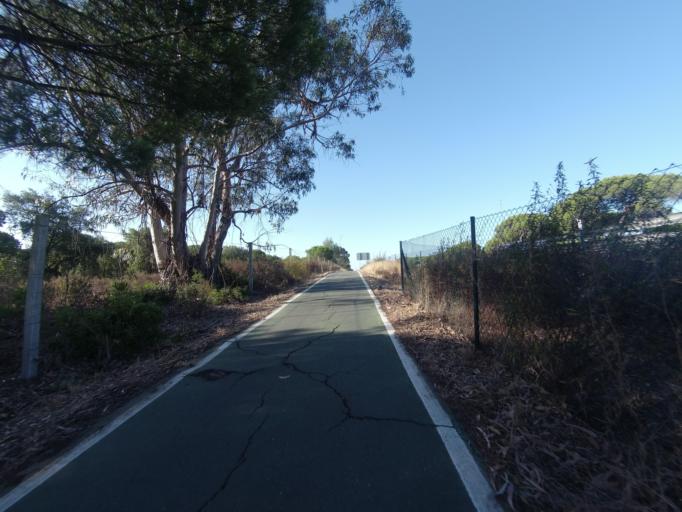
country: ES
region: Andalusia
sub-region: Provincia de Huelva
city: Aljaraque
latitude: 37.2417
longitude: -7.0183
